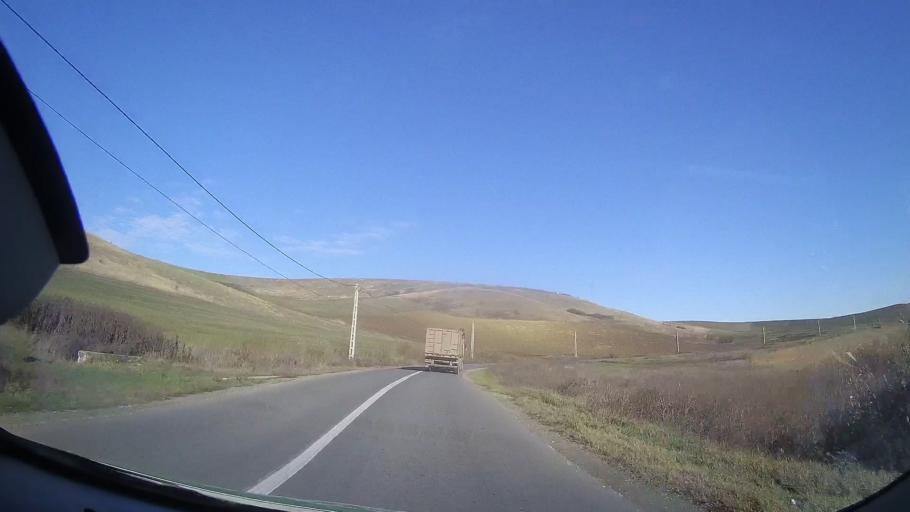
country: RO
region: Mures
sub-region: Comuna Mihesu de Campie
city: Mihesu de Campie
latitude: 46.6499
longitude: 24.1554
